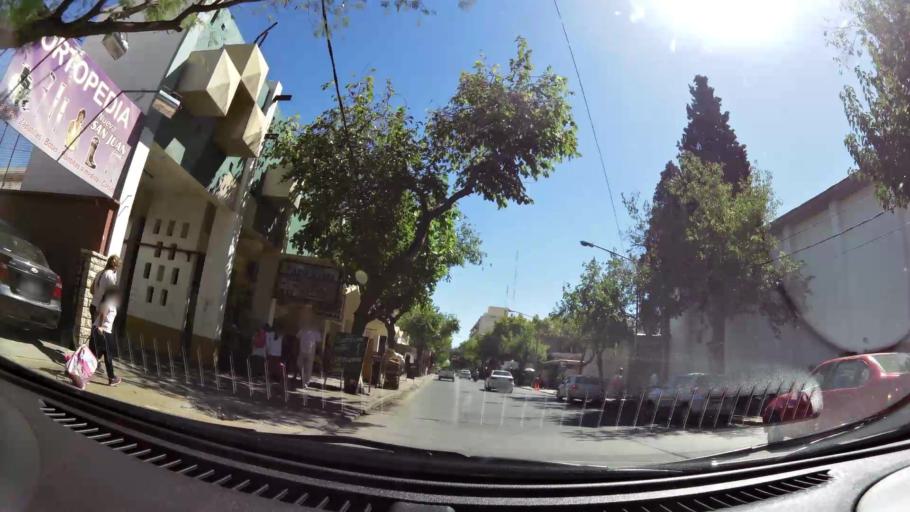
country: AR
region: San Juan
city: San Juan
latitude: -31.5398
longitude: -68.5242
